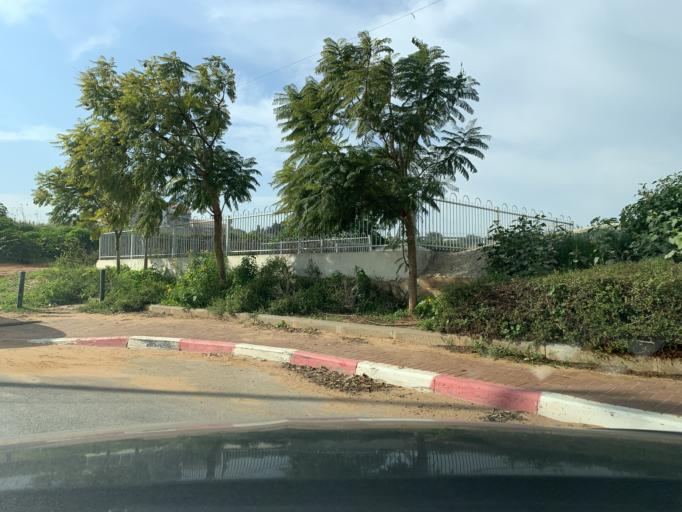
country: IL
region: Central District
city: Kfar Saba
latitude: 32.1856
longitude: 34.9253
